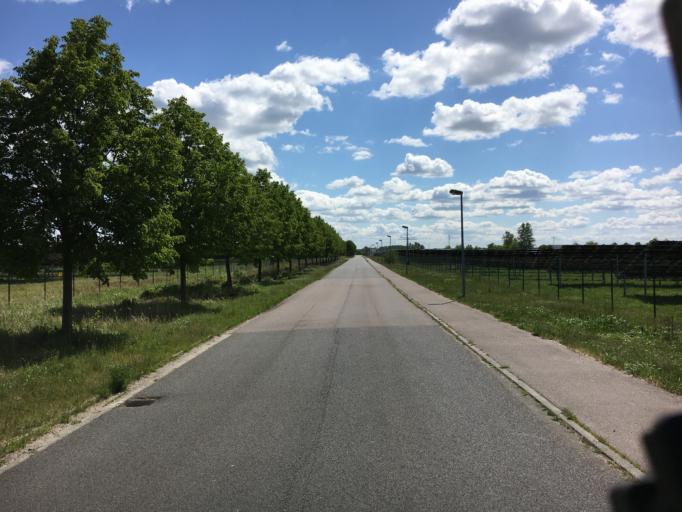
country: DE
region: Brandenburg
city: Trebbin
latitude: 52.1911
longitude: 13.2370
